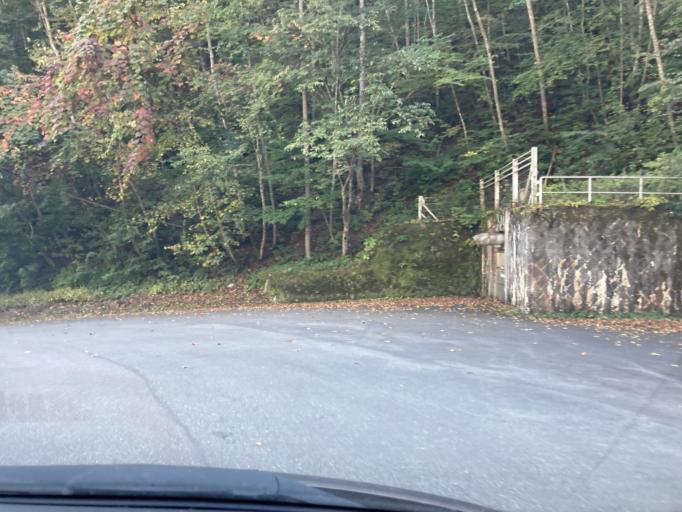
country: JP
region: Nagano
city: Omachi
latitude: 36.4891
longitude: 137.7376
